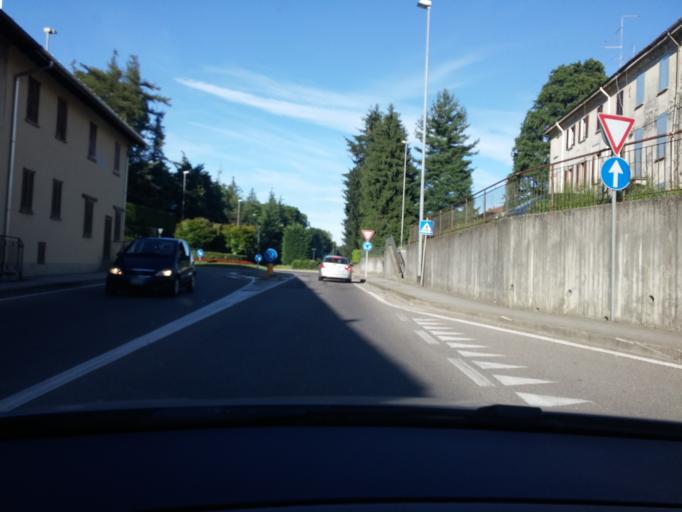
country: IT
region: Lombardy
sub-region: Provincia di Como
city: Cassina Rizzardi
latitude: 45.7524
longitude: 9.0175
